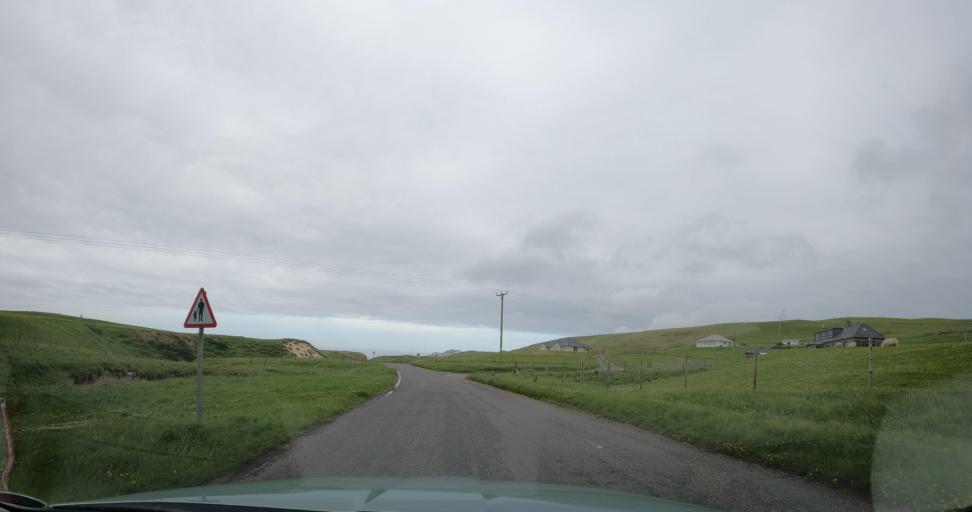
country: GB
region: Scotland
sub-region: Eilean Siar
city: Barra
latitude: 56.9723
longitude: -7.5154
